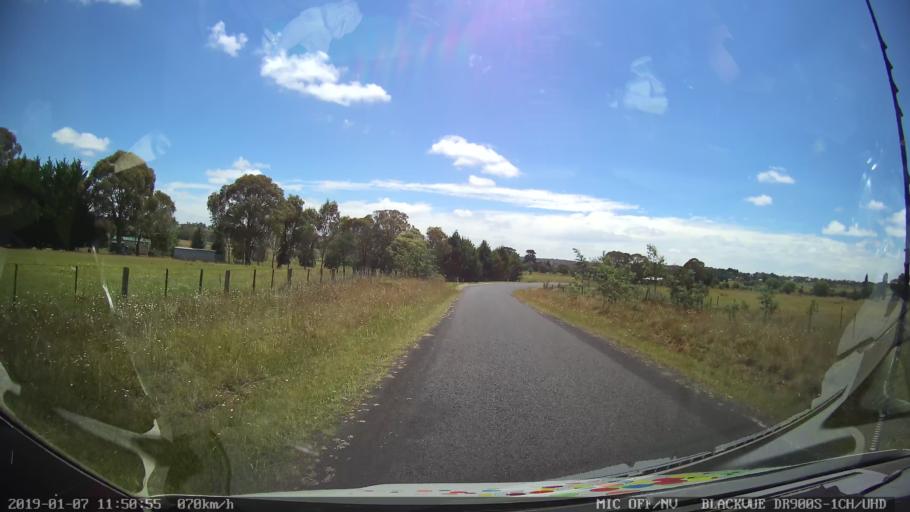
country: AU
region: New South Wales
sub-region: Guyra
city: Guyra
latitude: -30.3100
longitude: 151.6410
